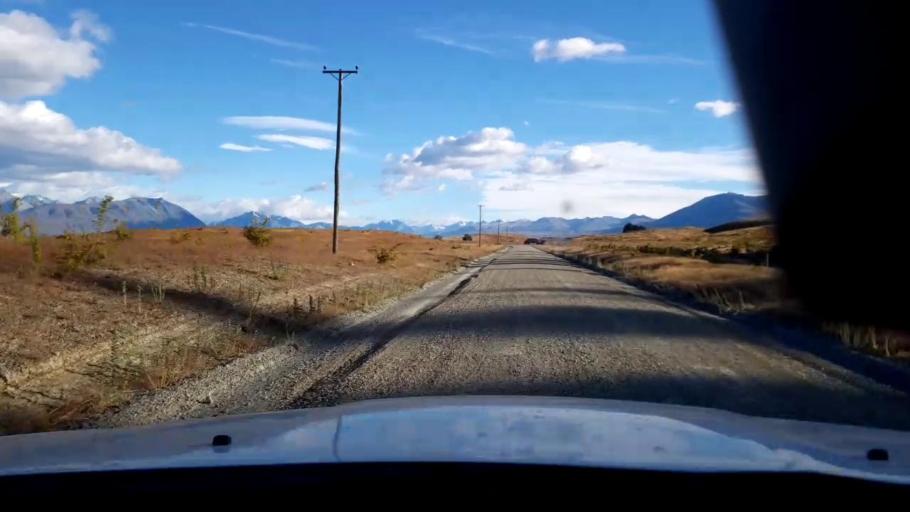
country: NZ
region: Canterbury
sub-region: Timaru District
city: Pleasant Point
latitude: -43.9804
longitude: 170.5093
